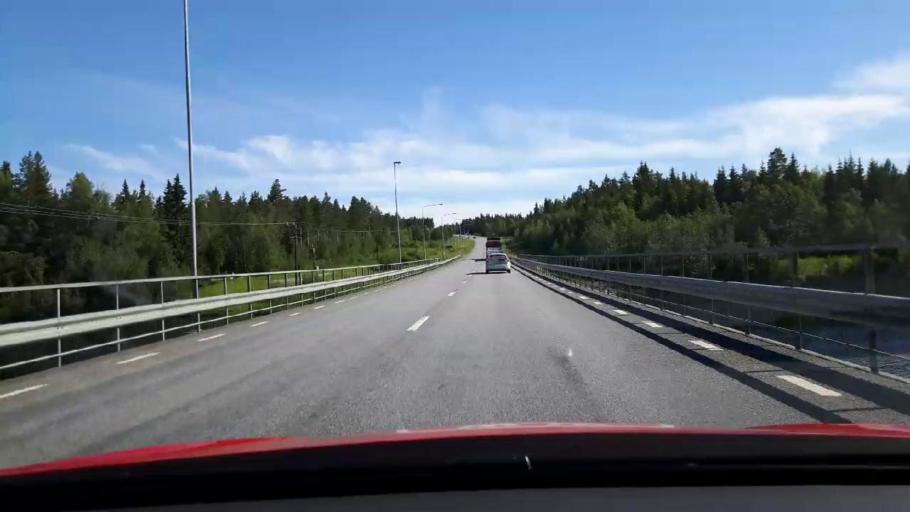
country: SE
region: Jaemtland
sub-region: OEstersunds Kommun
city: Lit
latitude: 63.3762
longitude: 14.8824
